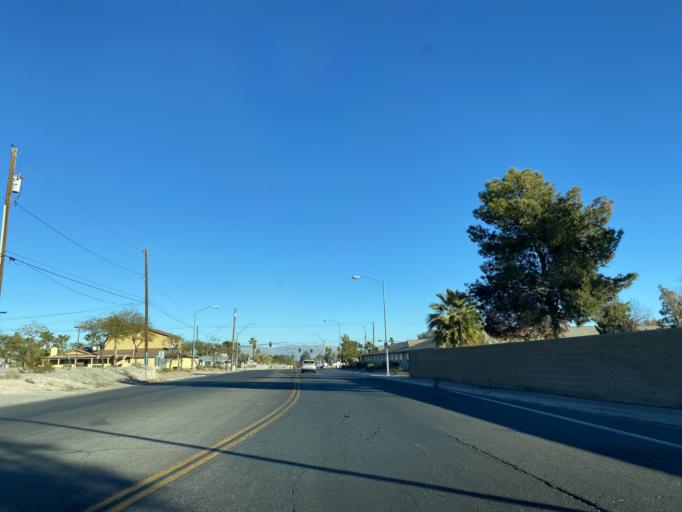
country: US
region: Nevada
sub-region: Clark County
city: Whitney
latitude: 36.0850
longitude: -115.1099
